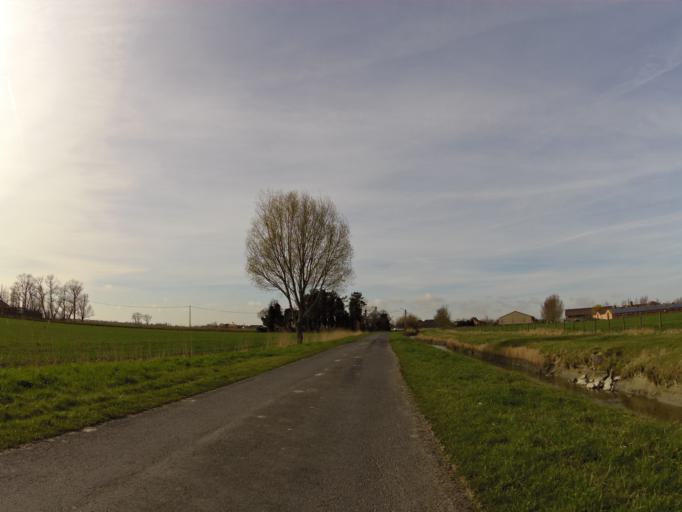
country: BE
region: Flanders
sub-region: Provincie West-Vlaanderen
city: Diksmuide
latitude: 51.0597
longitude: 2.8297
